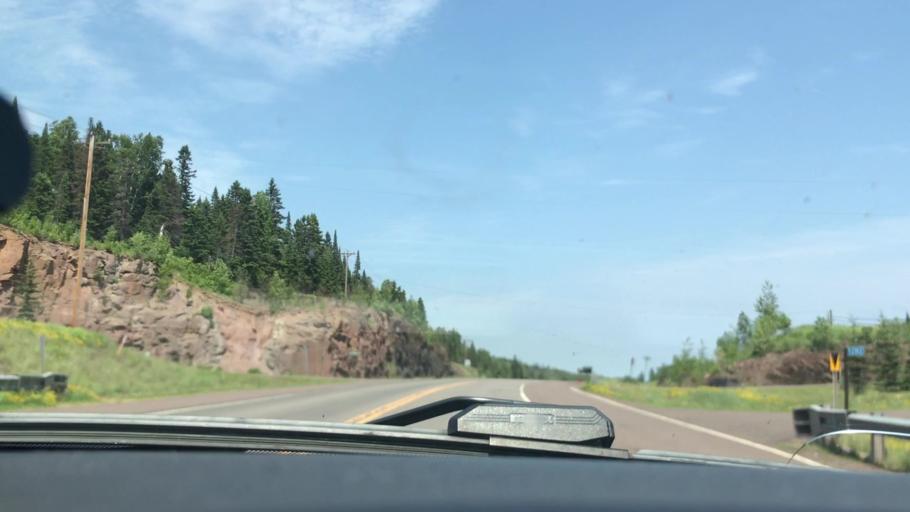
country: US
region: Minnesota
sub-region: Lake County
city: Silver Bay
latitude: 47.3088
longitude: -91.2390
